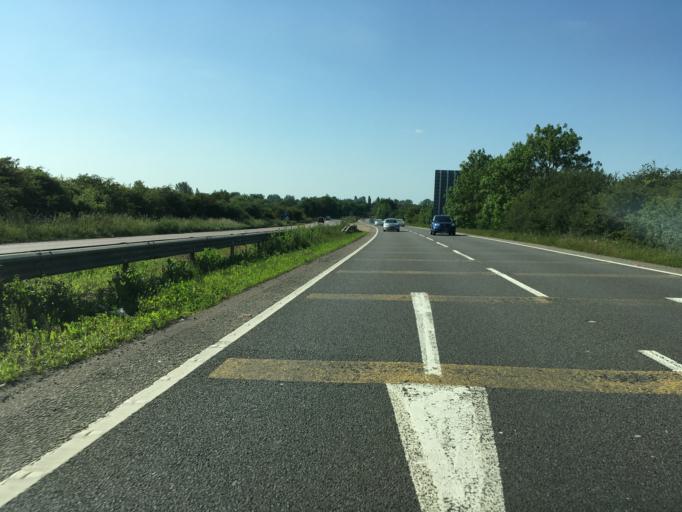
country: GB
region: England
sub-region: Milton Keynes
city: Water Eaton
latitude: 51.9948
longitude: -0.7026
